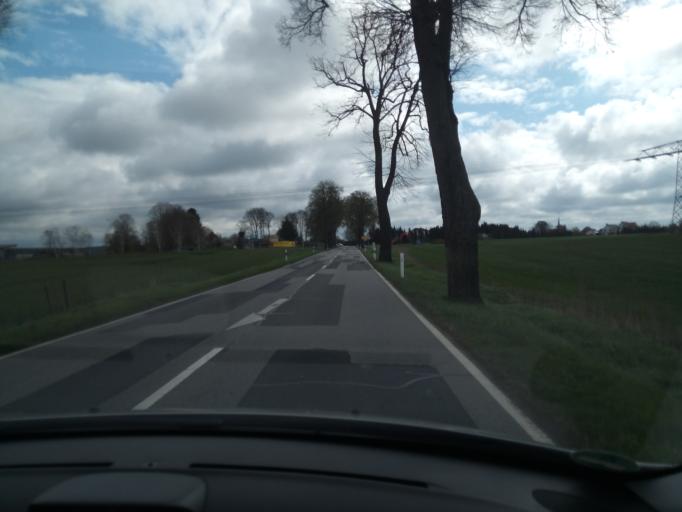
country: DE
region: Mecklenburg-Vorpommern
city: Burg Stargard
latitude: 53.5126
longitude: 13.2784
